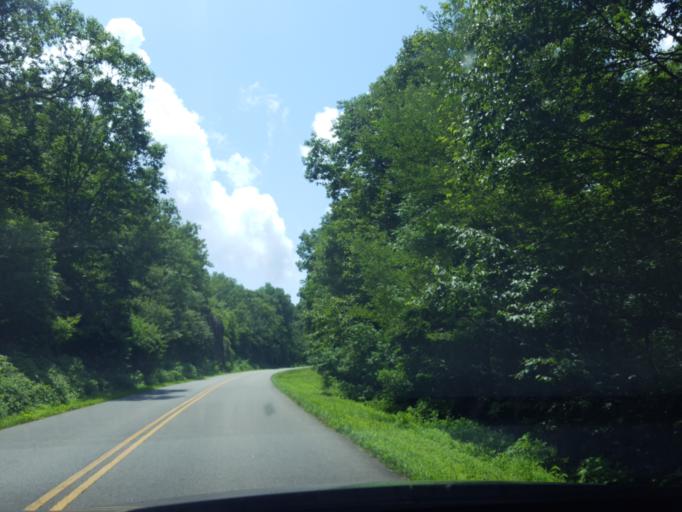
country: US
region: Virginia
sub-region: Nelson County
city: Nellysford
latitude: 37.9401
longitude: -78.9445
